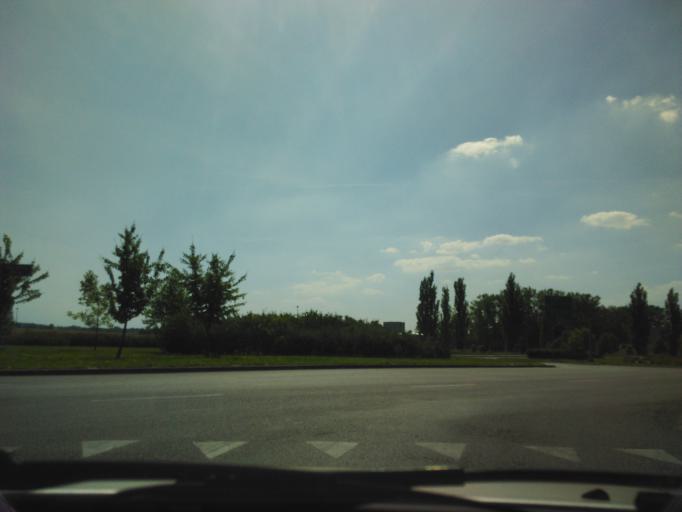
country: PL
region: West Pomeranian Voivodeship
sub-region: Powiat policki
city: Przeclaw
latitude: 53.3924
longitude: 14.5025
